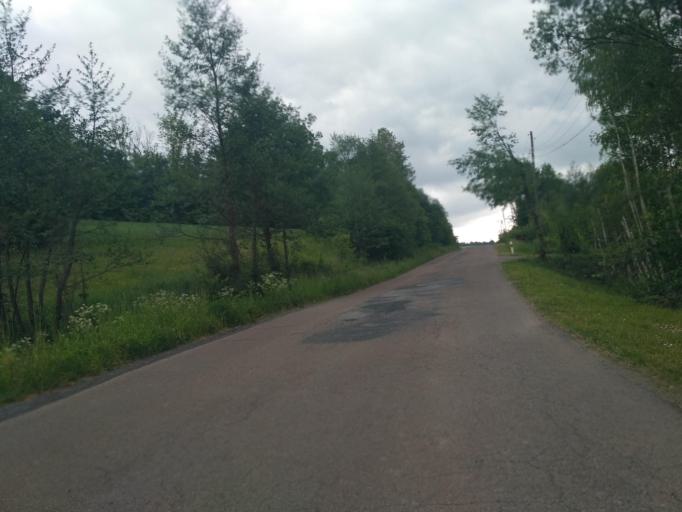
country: PL
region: Subcarpathian Voivodeship
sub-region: Powiat jasielski
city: Tarnowiec
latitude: 49.6780
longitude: 21.5863
